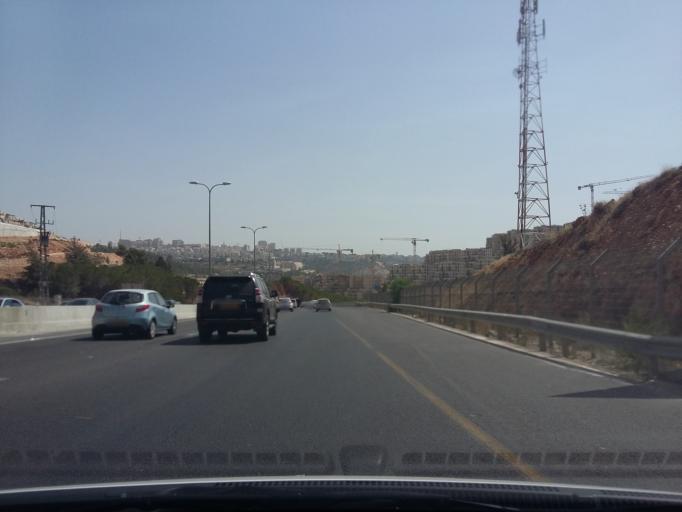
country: PS
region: West Bank
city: Bir Nabala
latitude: 31.8200
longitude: 35.2131
